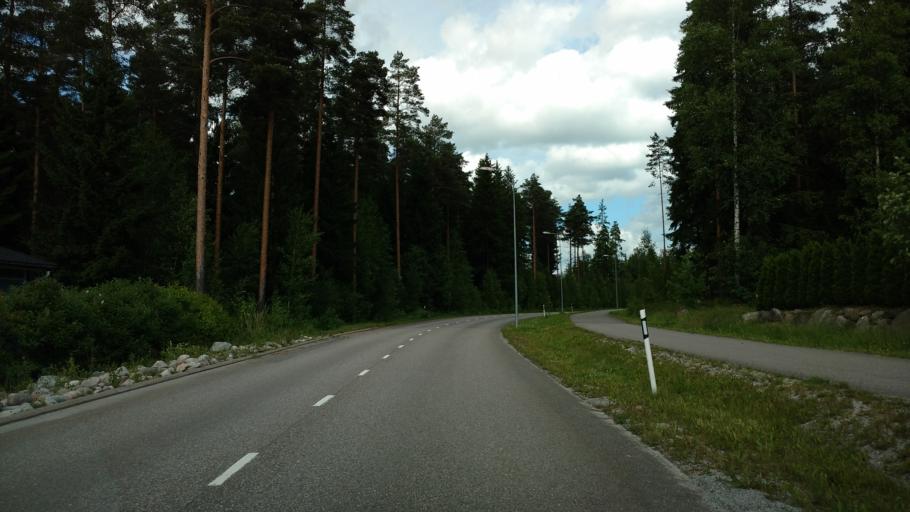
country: FI
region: Varsinais-Suomi
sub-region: Salo
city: Salo
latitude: 60.4055
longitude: 23.1833
